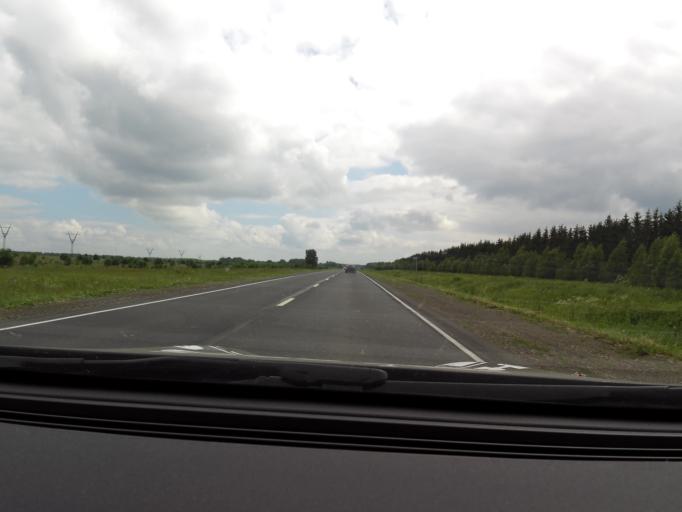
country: RU
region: Perm
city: Orda
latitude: 57.2449
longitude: 57.0490
